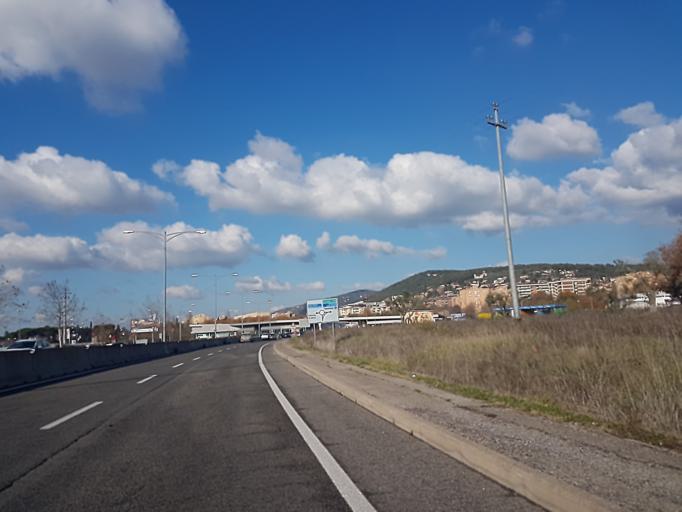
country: IT
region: Umbria
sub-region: Provincia di Perugia
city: Lacugnano
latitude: 43.0772
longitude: 12.3483
